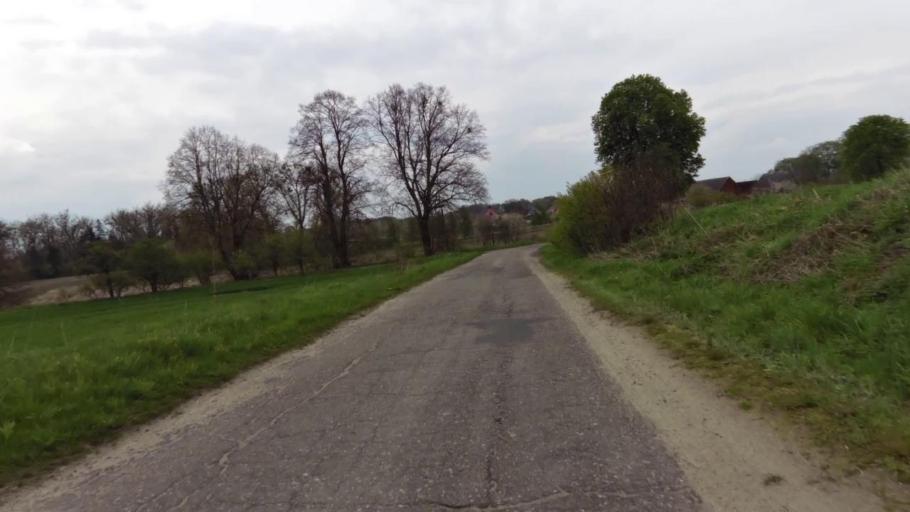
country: PL
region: West Pomeranian Voivodeship
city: Trzcinsko Zdroj
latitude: 52.9468
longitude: 14.7161
